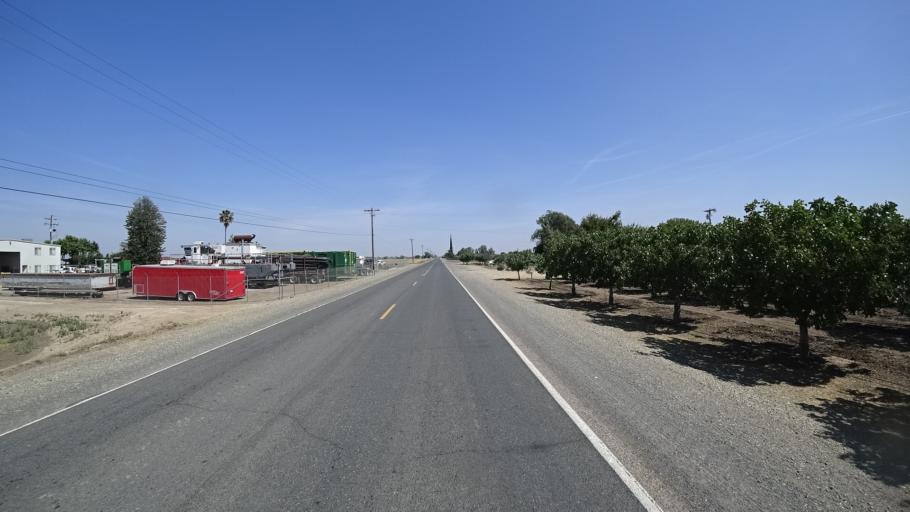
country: US
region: California
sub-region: Fresno County
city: Riverdale
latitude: 36.3935
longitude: -119.8512
